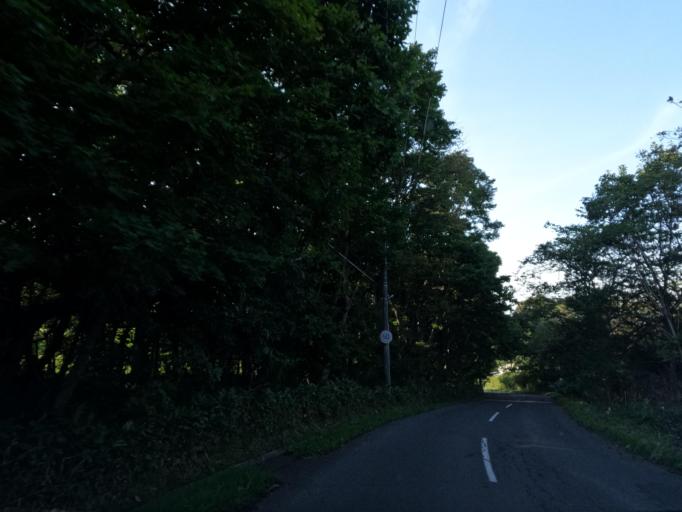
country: JP
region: Hokkaido
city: Date
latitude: 42.4106
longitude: 140.9159
